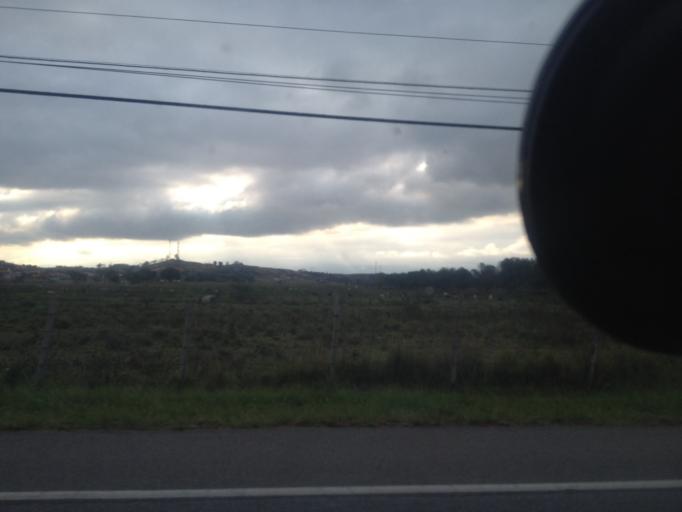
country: BR
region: Rio de Janeiro
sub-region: Porto Real
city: Porto Real
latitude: -22.4442
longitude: -44.3017
